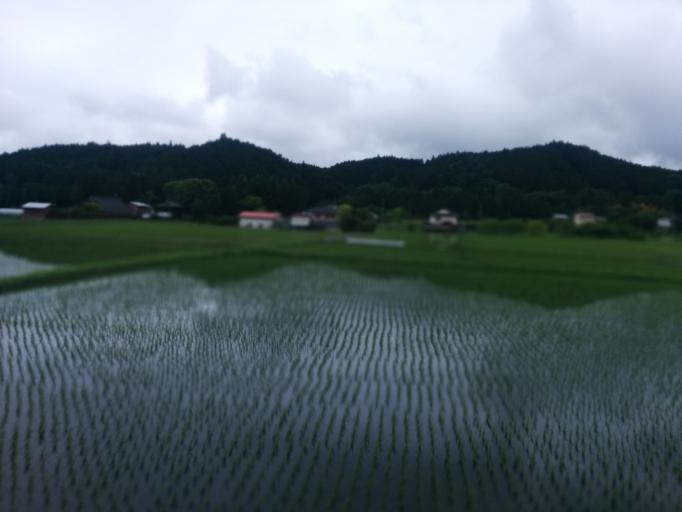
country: JP
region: Tochigi
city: Imaichi
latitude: 36.7258
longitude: 139.6734
